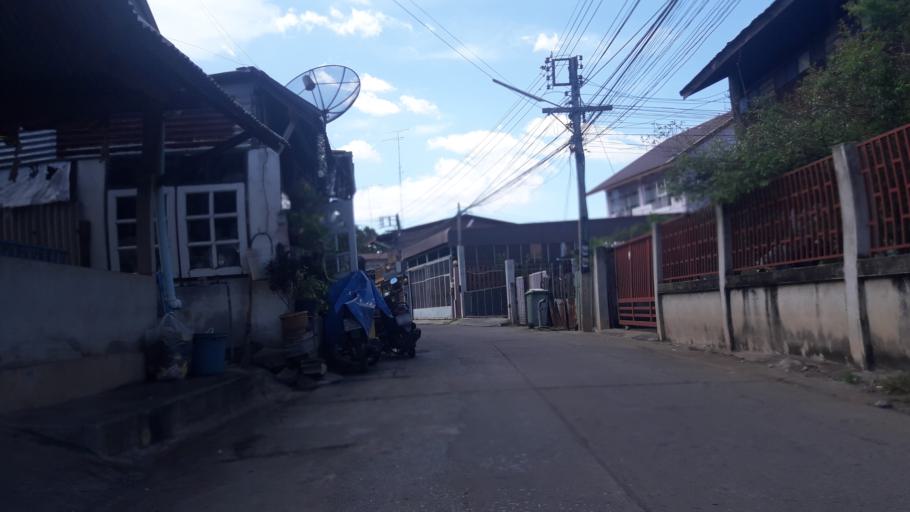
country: TH
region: Phichit
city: Thap Khlo
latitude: 16.1695
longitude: 100.5782
